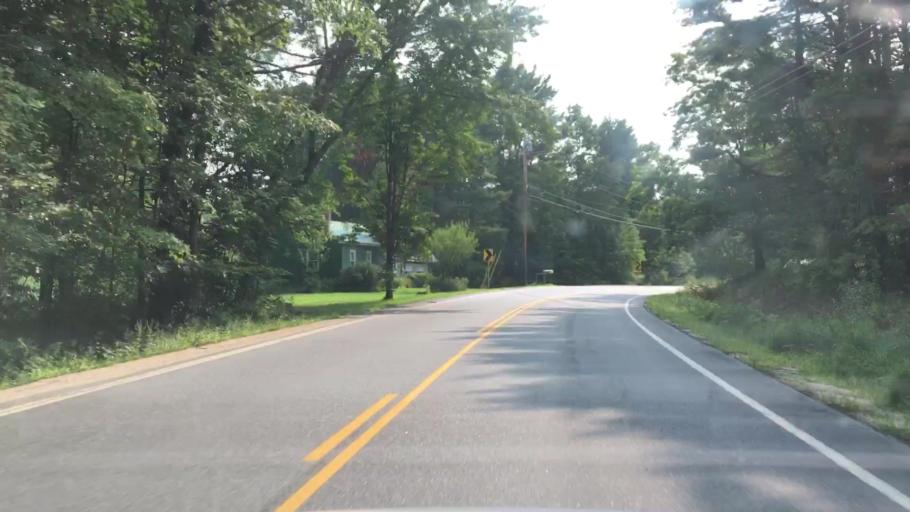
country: US
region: Maine
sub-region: Oxford County
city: South Paris
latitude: 44.2246
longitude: -70.4982
